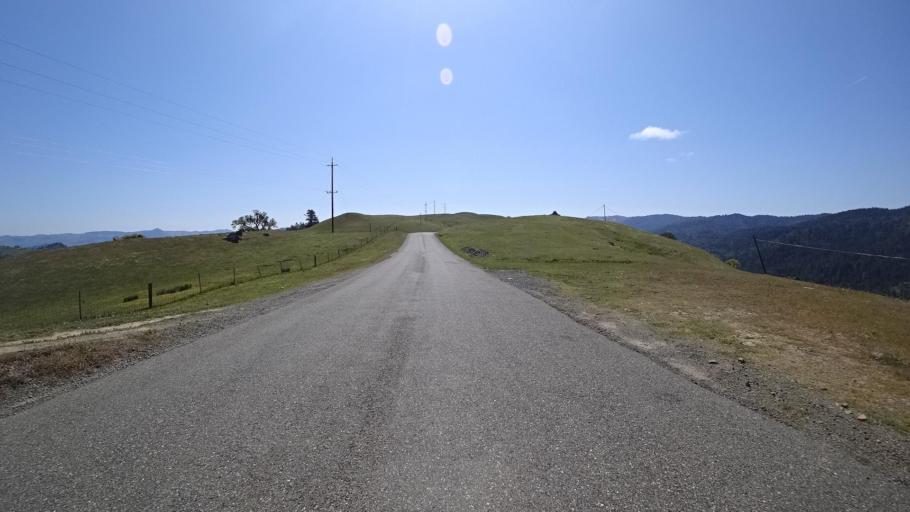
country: US
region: California
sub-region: Humboldt County
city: Redway
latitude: 40.0293
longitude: -123.6353
